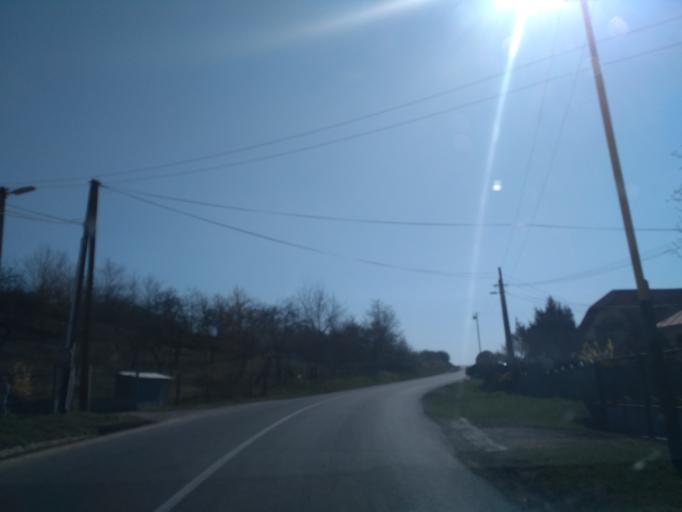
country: HU
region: Borsod-Abauj-Zemplen
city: Gonc
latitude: 48.5968
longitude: 21.3494
